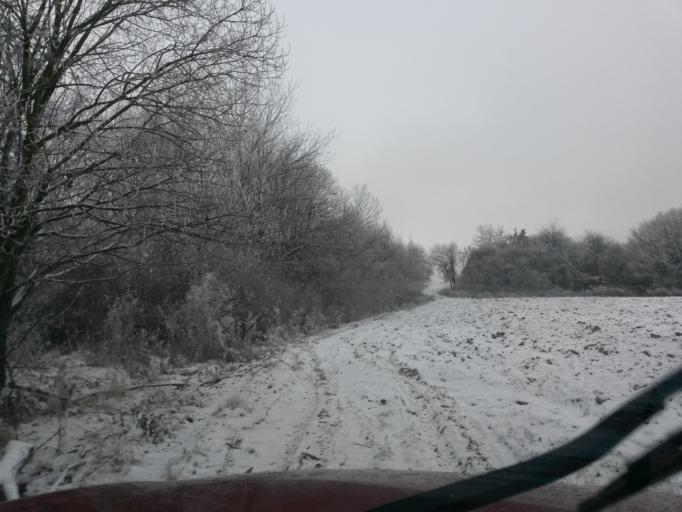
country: SK
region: Presovsky
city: Sabinov
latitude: 48.9820
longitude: 21.0806
